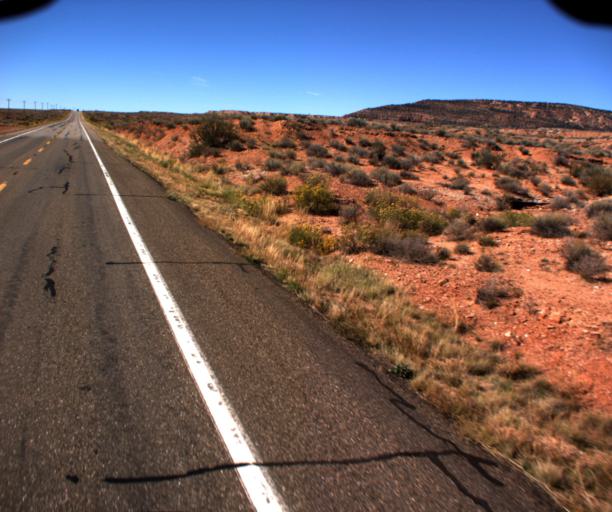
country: US
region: Arizona
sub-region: Coconino County
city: Fredonia
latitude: 36.8631
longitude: -112.7103
